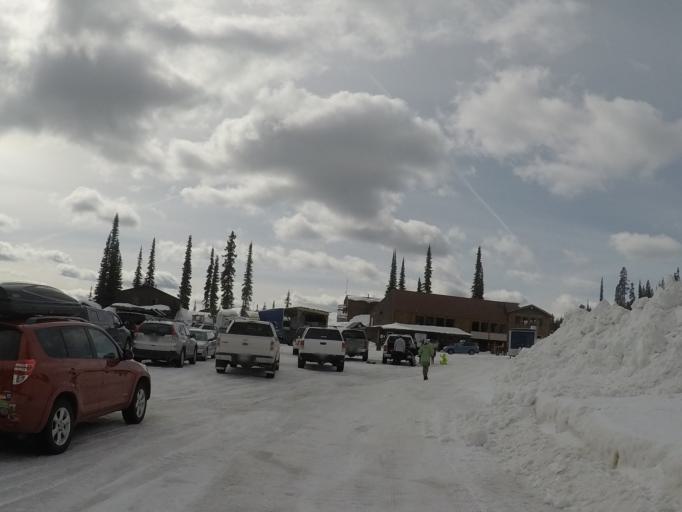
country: US
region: Idaho
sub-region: Lemhi County
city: Salmon
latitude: 45.6929
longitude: -113.9522
